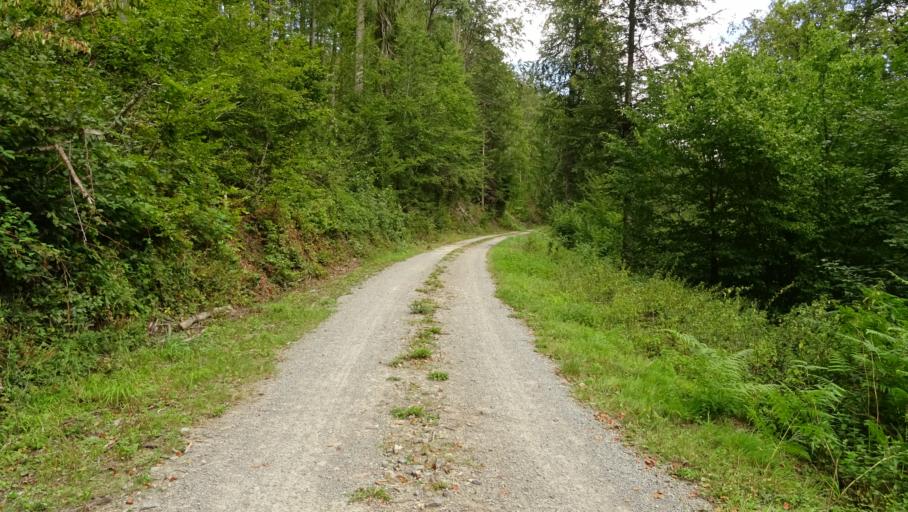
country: DE
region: Baden-Wuerttemberg
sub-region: Karlsruhe Region
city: Fahrenbach
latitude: 49.4314
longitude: 9.1213
